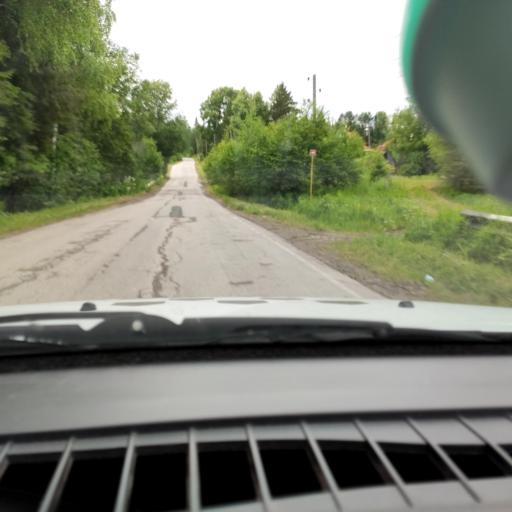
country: RU
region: Perm
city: Lys'va
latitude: 58.1165
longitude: 57.6976
